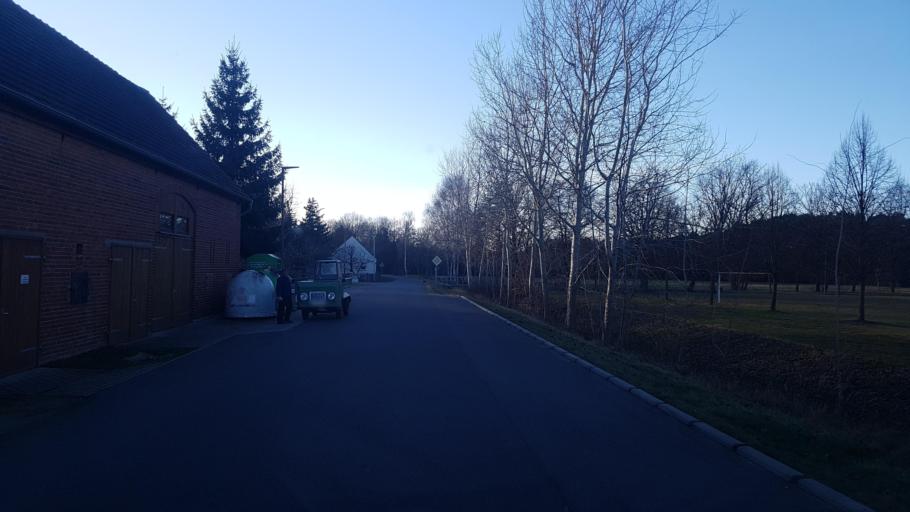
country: DE
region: Brandenburg
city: Drehnow
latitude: 51.8742
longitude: 14.3855
